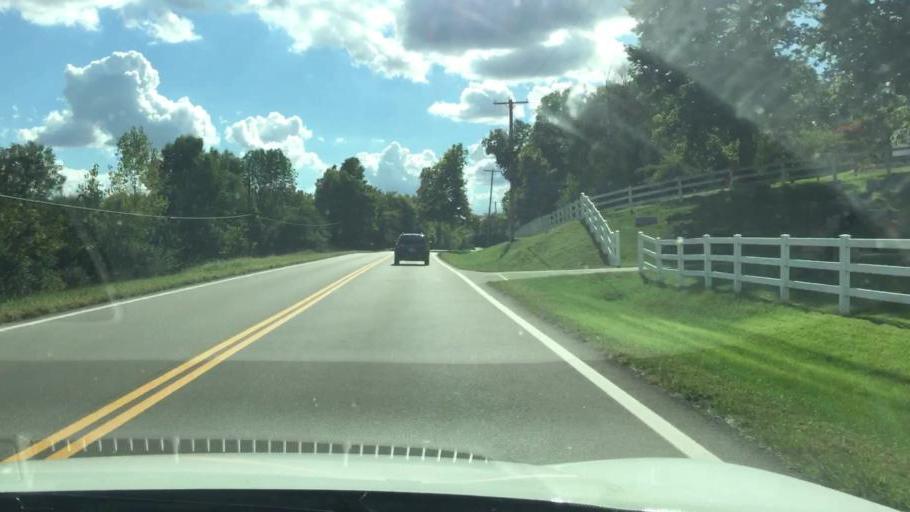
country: US
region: Ohio
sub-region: Clark County
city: Northridge
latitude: 39.9818
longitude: -83.7374
